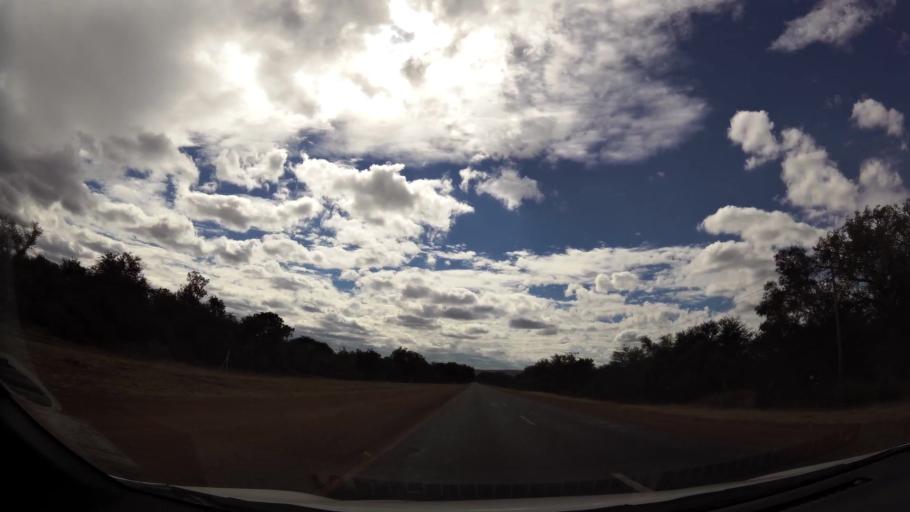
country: ZA
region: Limpopo
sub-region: Waterberg District Municipality
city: Warmbaths
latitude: -24.8944
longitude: 28.2821
